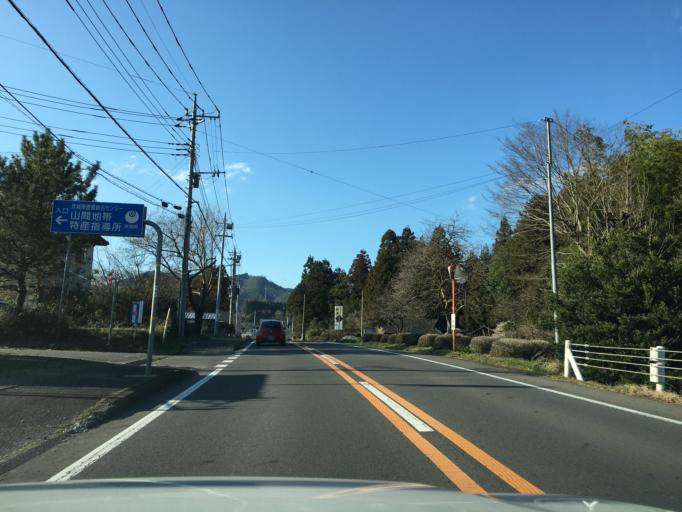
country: JP
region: Ibaraki
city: Daigo
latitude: 36.7150
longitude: 140.3866
